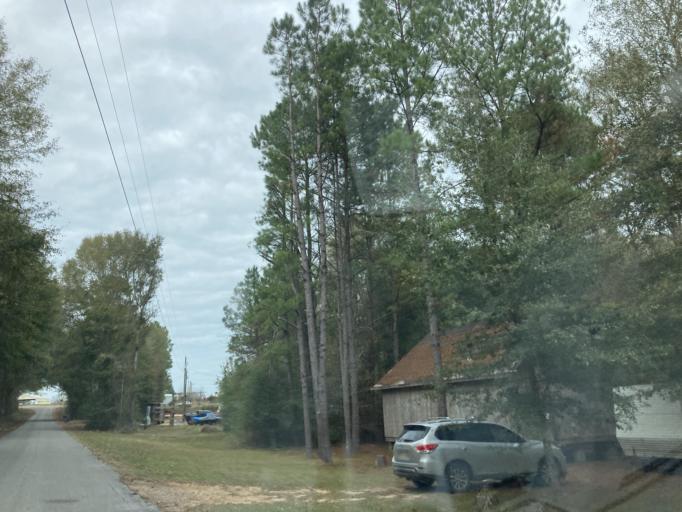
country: US
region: Mississippi
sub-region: Stone County
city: Wiggins
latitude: 31.0634
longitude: -89.2057
